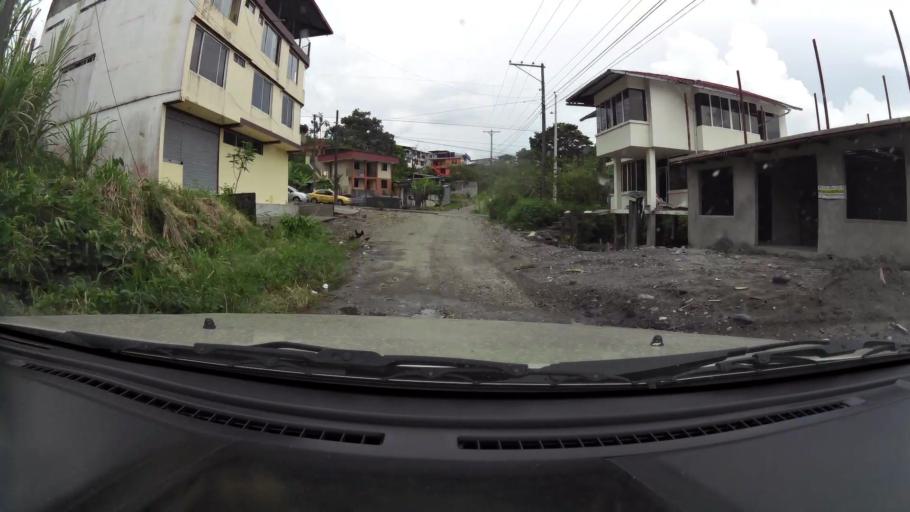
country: EC
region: Pastaza
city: Puyo
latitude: -1.4920
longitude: -78.0062
